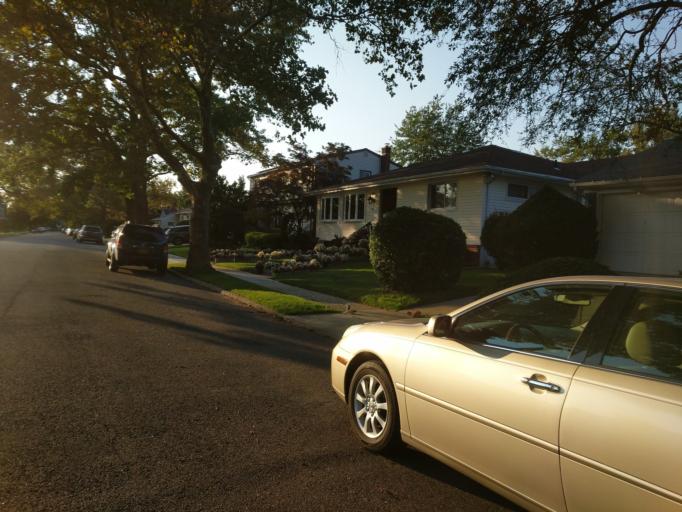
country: US
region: New York
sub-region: Nassau County
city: South Valley Stream
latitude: 40.6576
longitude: -73.7159
